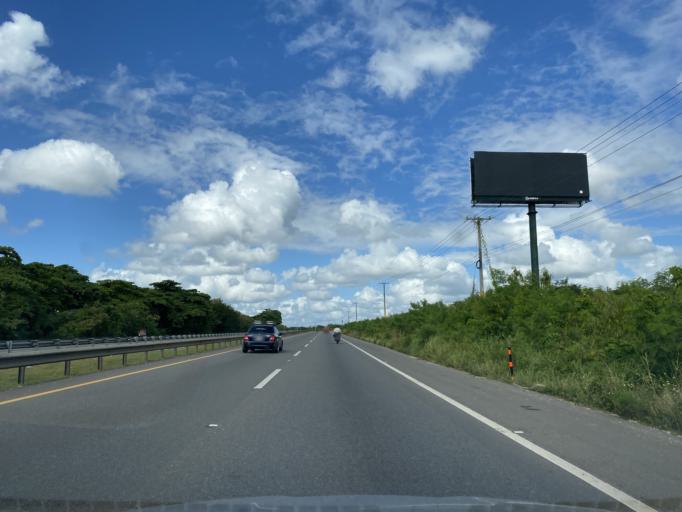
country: DO
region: Santo Domingo
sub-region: Santo Domingo
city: Boca Chica
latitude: 18.4400
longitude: -69.5798
